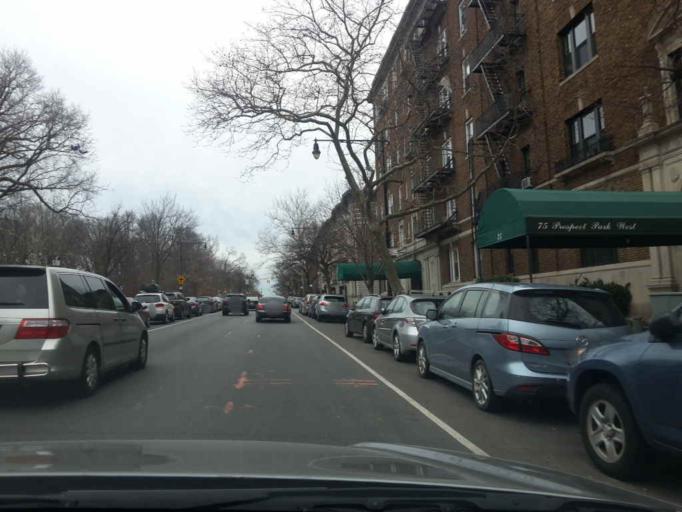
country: US
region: New York
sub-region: Kings County
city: Brooklyn
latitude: 40.6682
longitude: -73.9739
